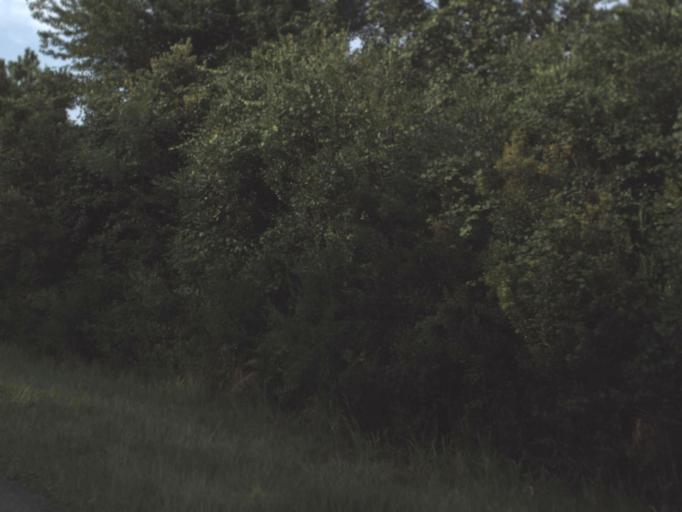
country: US
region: Florida
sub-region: Taylor County
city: Perry
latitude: 30.3104
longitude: -83.6385
